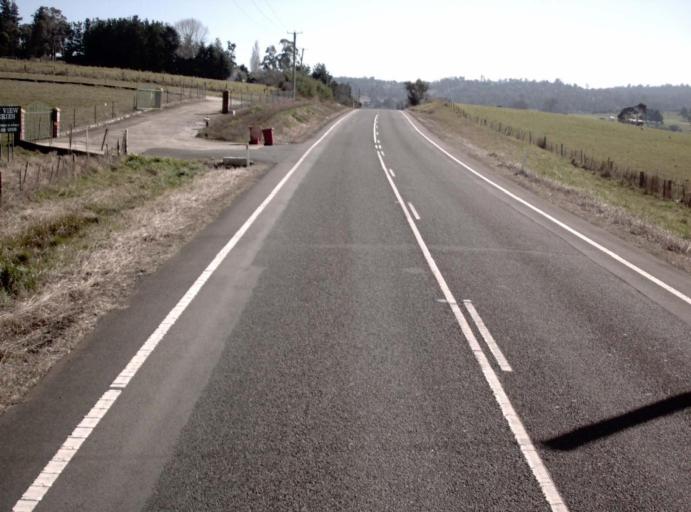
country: AU
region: Tasmania
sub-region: Launceston
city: Mayfield
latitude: -41.3228
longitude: 147.0619
